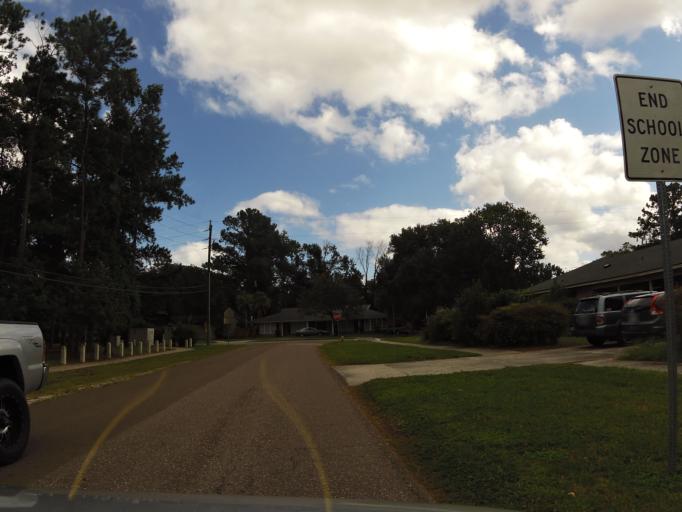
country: US
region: Florida
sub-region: Duval County
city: Jacksonville
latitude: 30.2593
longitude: -81.7037
